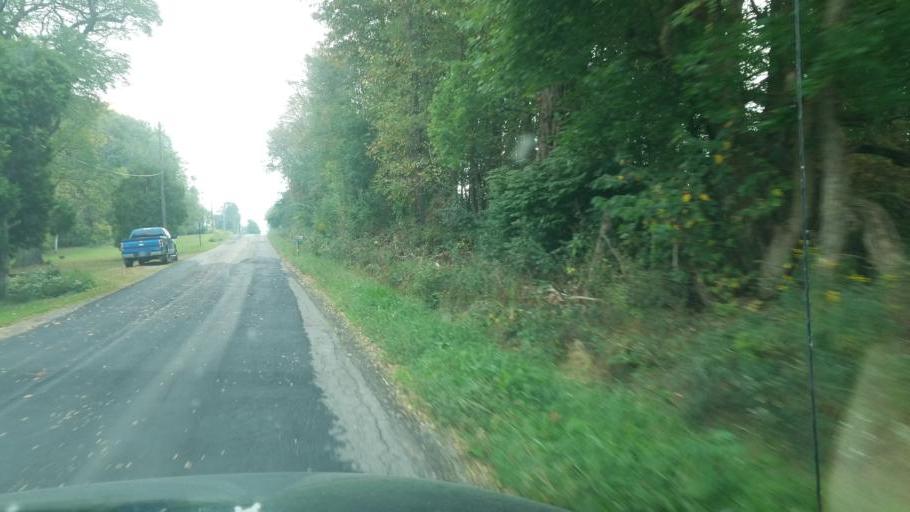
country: US
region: Ohio
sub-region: Knox County
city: Centerburg
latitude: 40.3480
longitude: -82.6386
